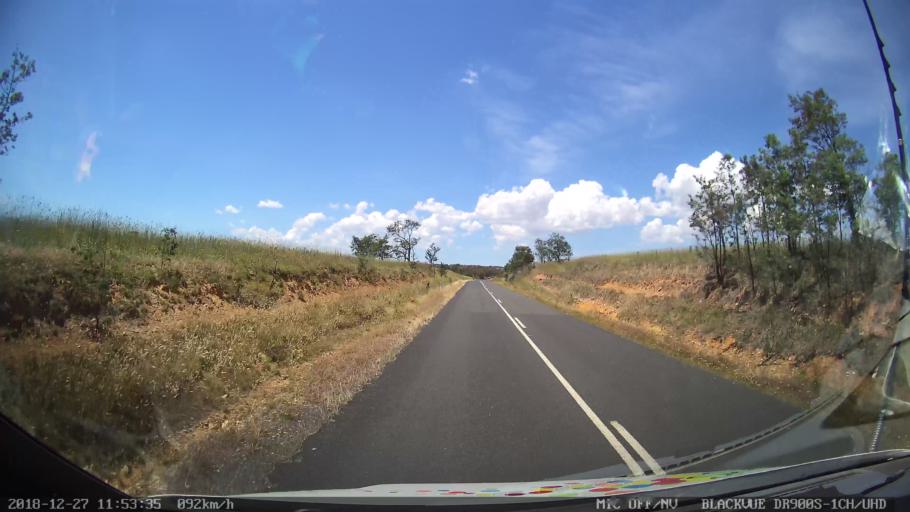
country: AU
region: New South Wales
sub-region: Blayney
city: Blayney
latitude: -33.6638
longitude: 149.4018
